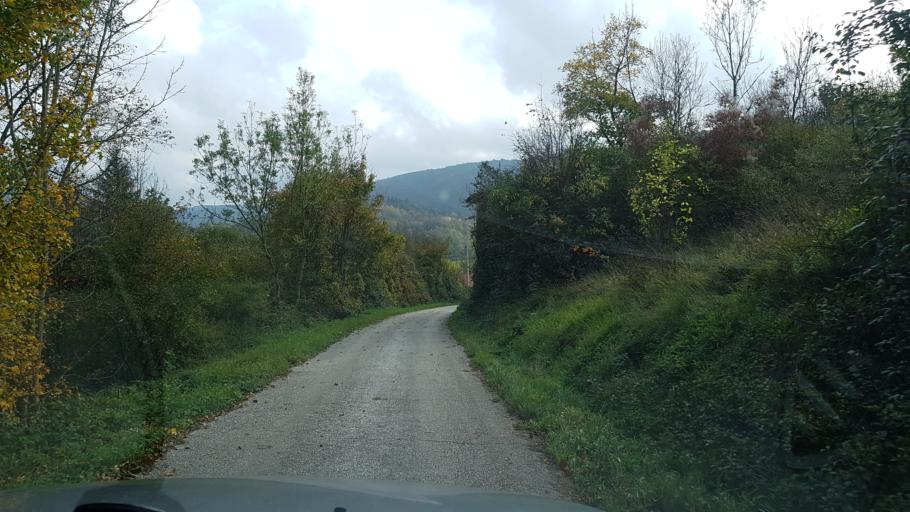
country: HR
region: Istarska
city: Buzet
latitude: 45.4254
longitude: 14.0733
